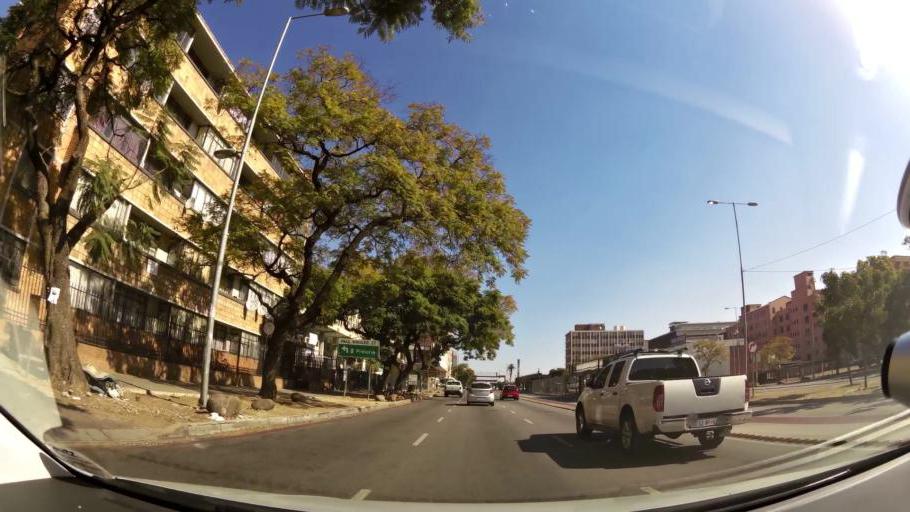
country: ZA
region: Gauteng
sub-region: City of Tshwane Metropolitan Municipality
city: Pretoria
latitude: -25.7507
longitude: 28.1900
